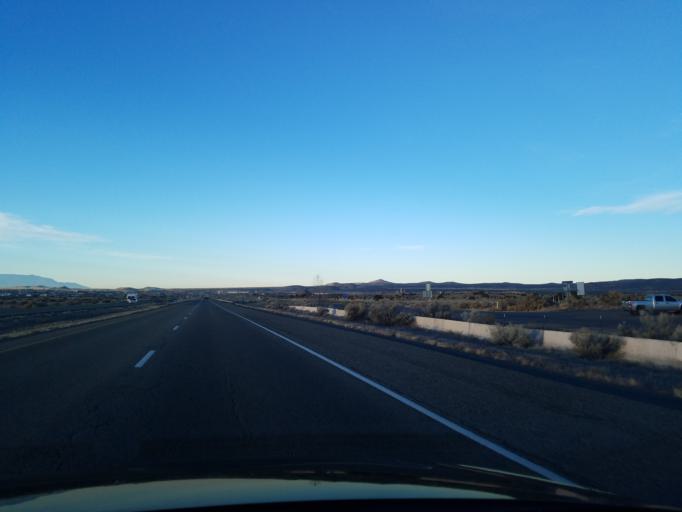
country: US
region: New Mexico
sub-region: Santa Fe County
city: Agua Fria
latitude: 35.6473
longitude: -106.0552
